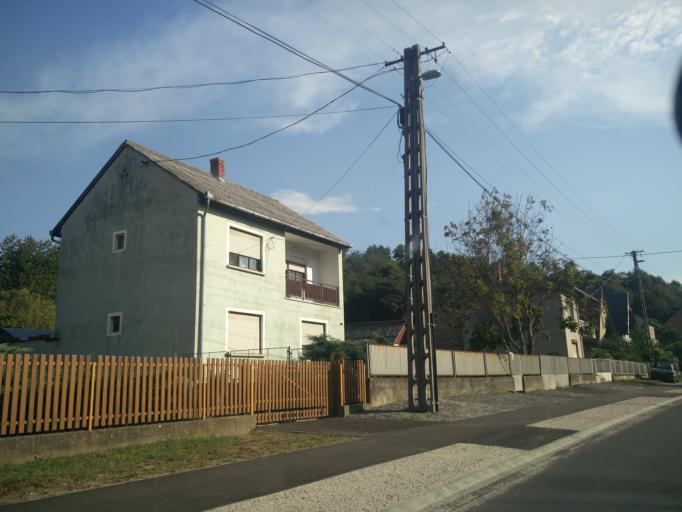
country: HU
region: Zala
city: Zalaegerszeg
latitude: 46.8493
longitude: 16.7989
